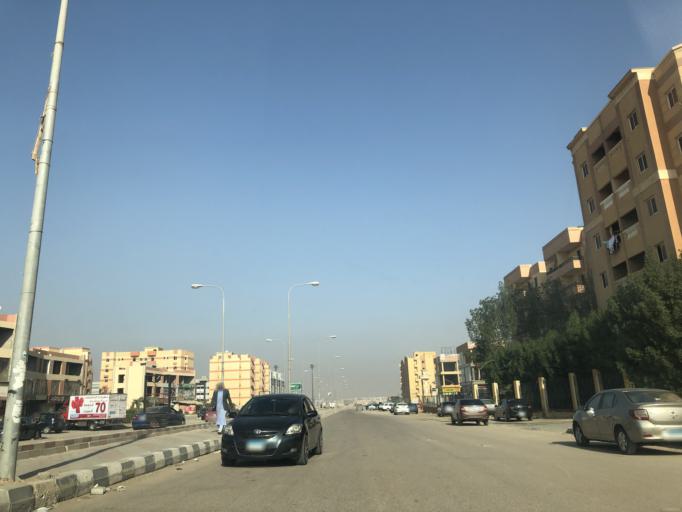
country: EG
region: Al Jizah
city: Madinat Sittah Uktubar
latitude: 29.9127
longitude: 31.0602
